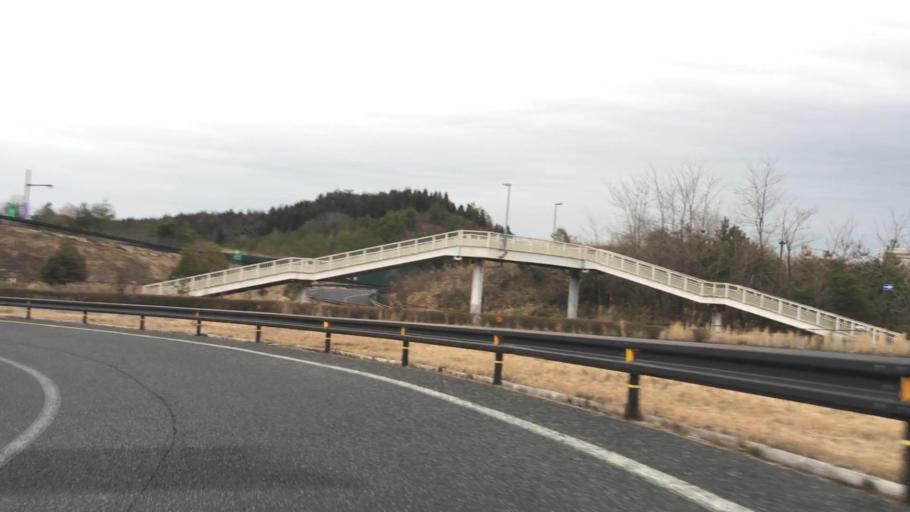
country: JP
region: Gifu
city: Toki
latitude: 35.3315
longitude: 137.1699
